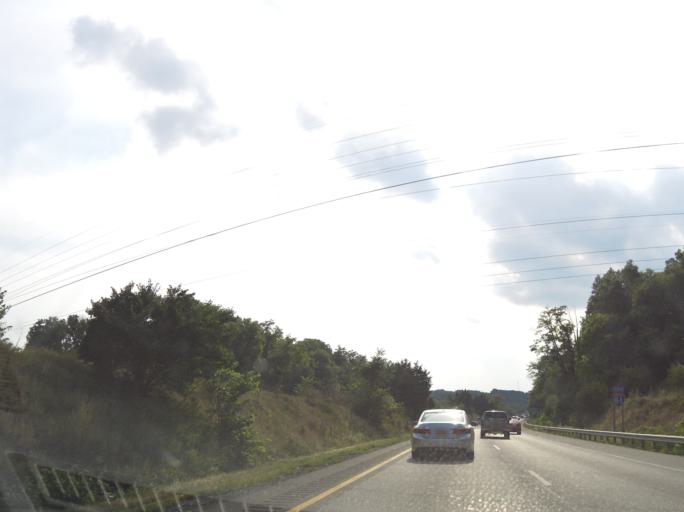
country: US
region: Maryland
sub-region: Washington County
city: Williamsport
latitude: 39.5848
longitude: -77.8243
